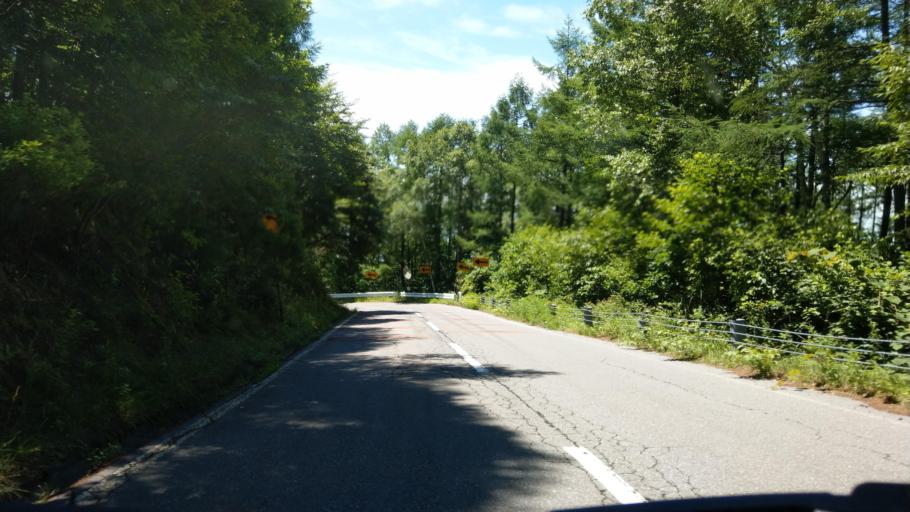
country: JP
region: Nagano
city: Komoro
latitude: 36.3915
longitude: 138.4666
